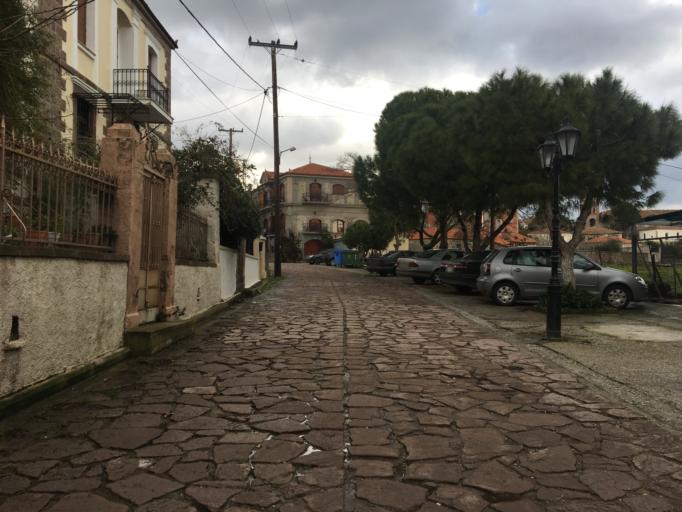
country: GR
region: North Aegean
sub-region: Nomos Lesvou
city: Agia Paraskevi
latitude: 39.2466
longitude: 26.2695
